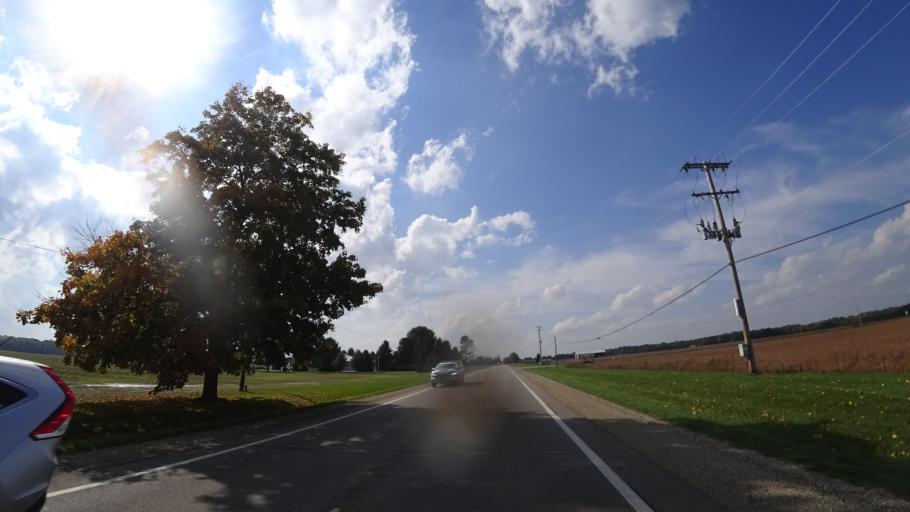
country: US
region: Michigan
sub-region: Saint Joseph County
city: Centreville
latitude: 42.0063
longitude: -85.4818
